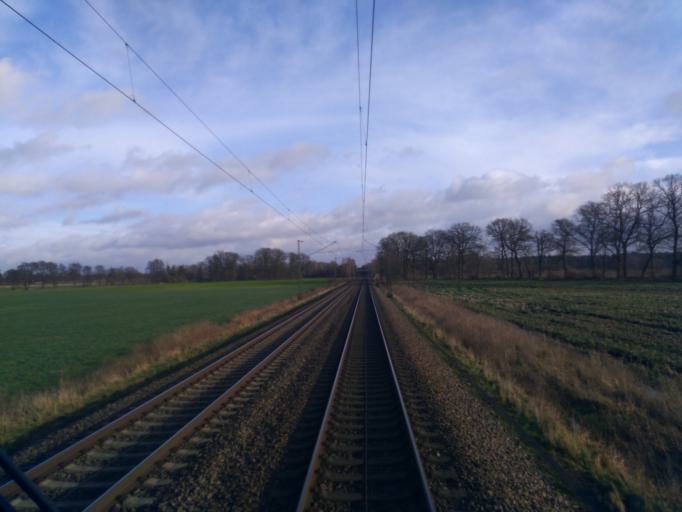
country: DE
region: Lower Saxony
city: Hassendorf
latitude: 53.1023
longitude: 9.2969
